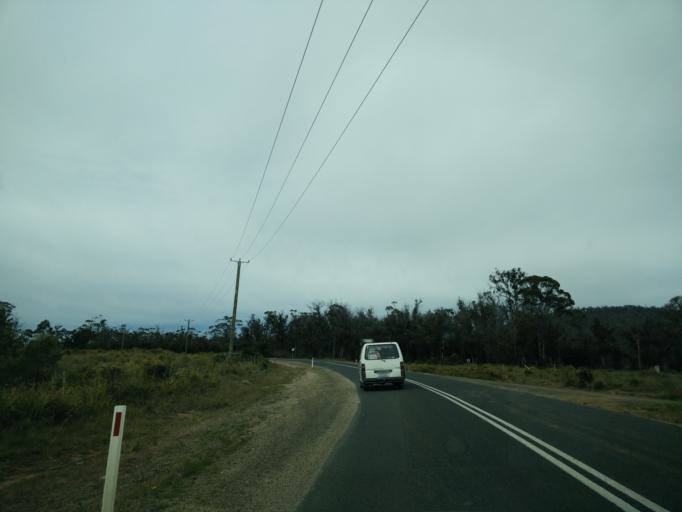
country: AU
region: Tasmania
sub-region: Break O'Day
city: St Helens
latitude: -41.8962
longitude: 148.2559
